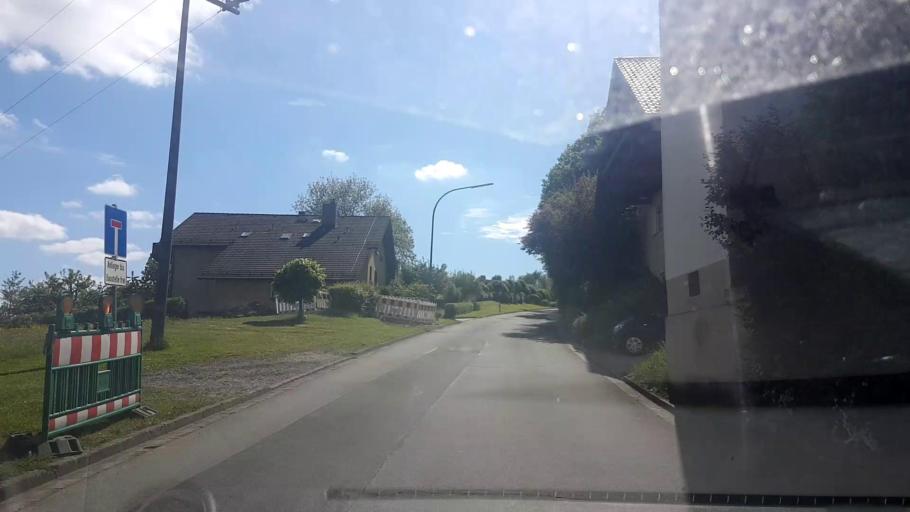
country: DE
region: Bavaria
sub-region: Regierungsbezirk Unterfranken
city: Untermerzbach
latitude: 50.1524
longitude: 10.8997
